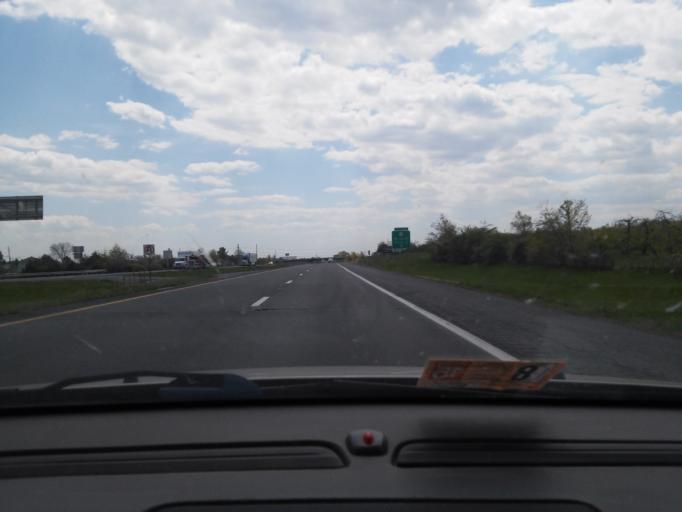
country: US
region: West Virginia
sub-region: Berkeley County
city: Inwood
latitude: 39.2965
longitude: -78.0809
